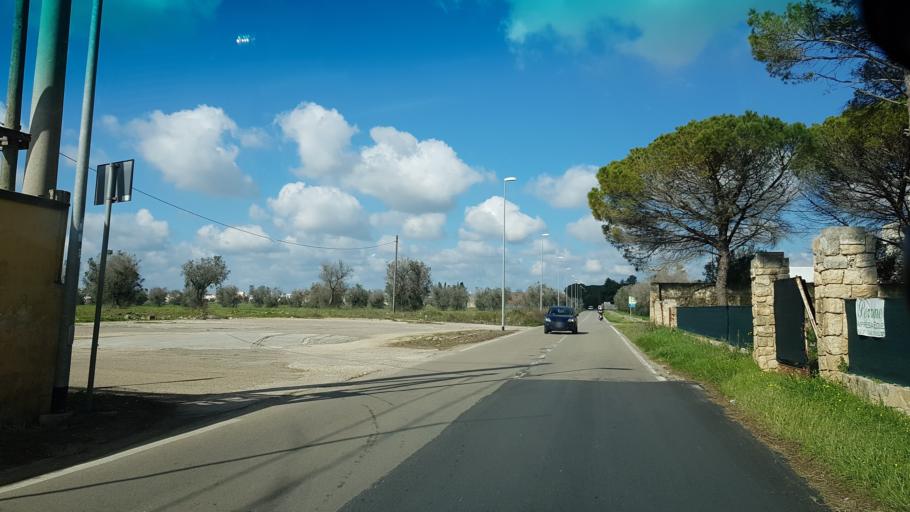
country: IT
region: Apulia
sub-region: Provincia di Lecce
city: Campi Salentina
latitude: 40.3921
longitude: 18.0312
